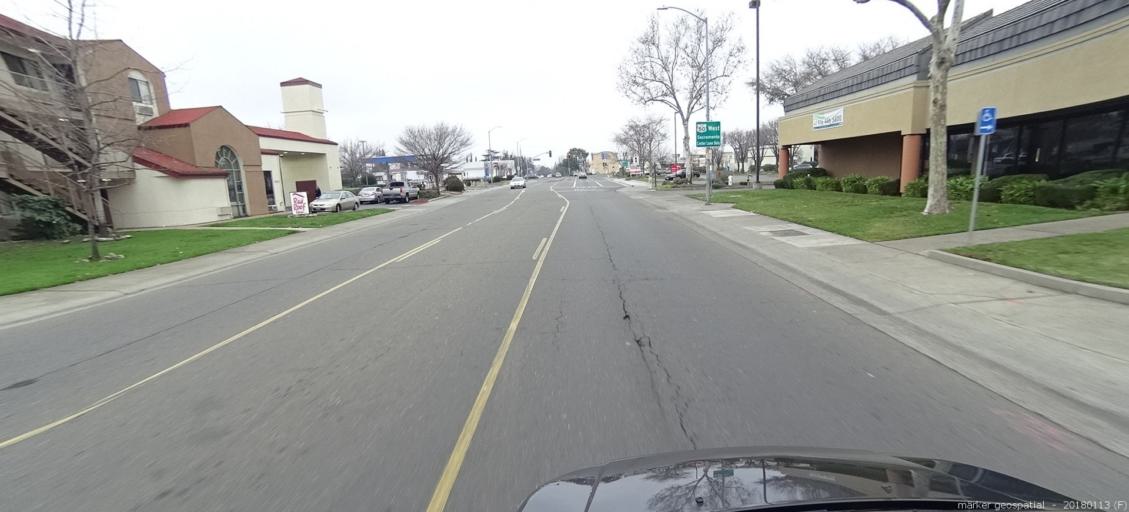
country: US
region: California
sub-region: Sacramento County
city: Rancho Cordova
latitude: 38.5938
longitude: -121.2860
